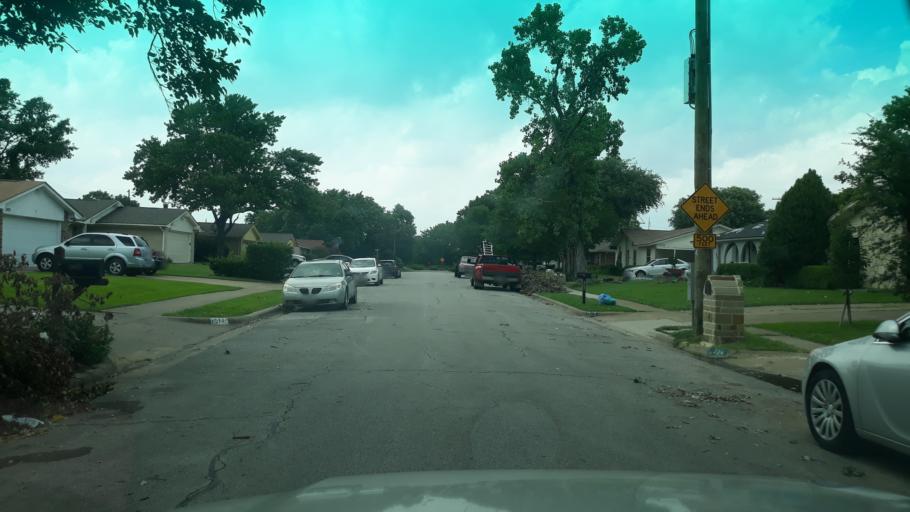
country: US
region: Texas
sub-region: Dallas County
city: Irving
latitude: 32.8540
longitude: -96.9948
